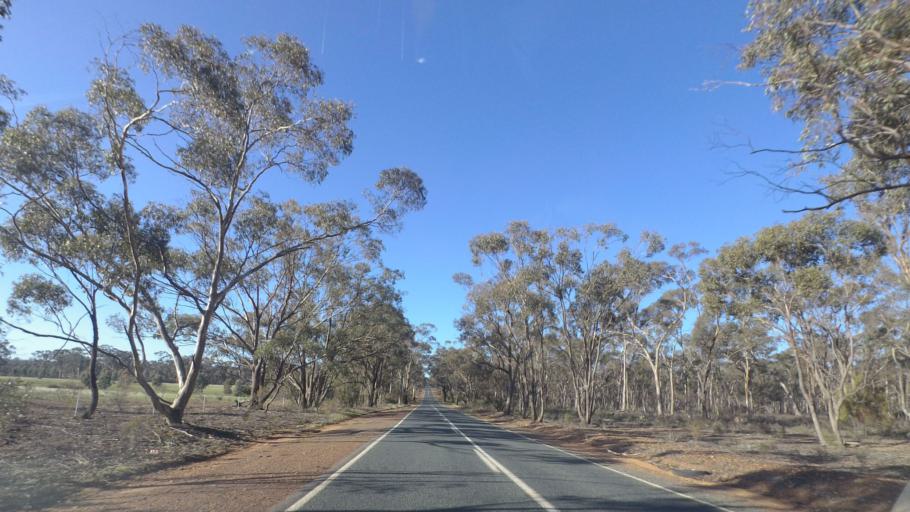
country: AU
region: Victoria
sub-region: Greater Bendigo
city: Epsom
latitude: -36.6702
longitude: 144.4183
